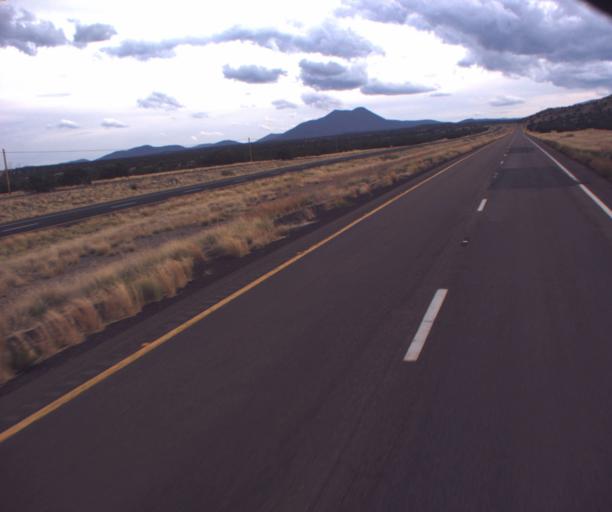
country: US
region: Arizona
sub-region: Coconino County
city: Flagstaff
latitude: 35.5337
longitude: -111.5409
